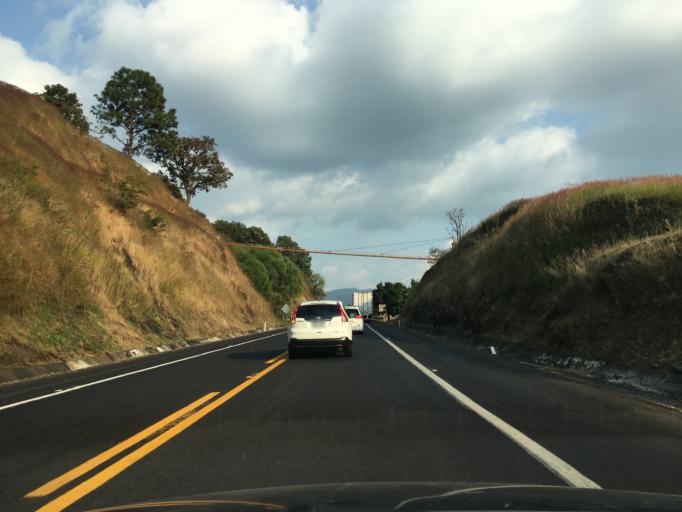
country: MX
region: Michoacan
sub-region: Ziracuaretiro
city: Patuan
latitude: 19.4327
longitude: -101.8982
